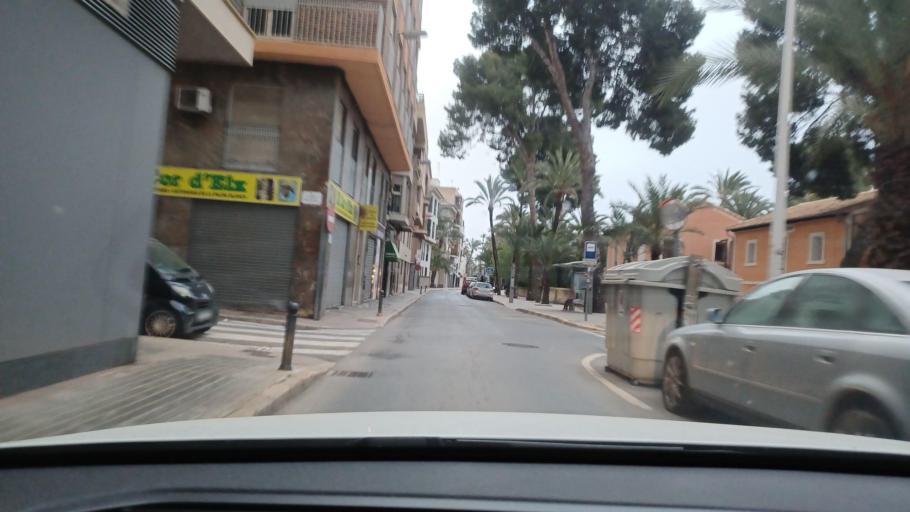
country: ES
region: Valencia
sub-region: Provincia de Alicante
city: Elche
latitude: 38.2643
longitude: -0.6938
